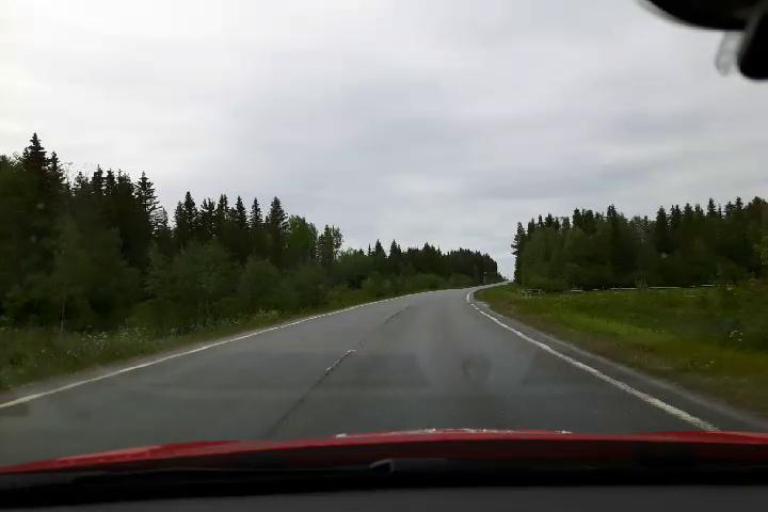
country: SE
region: Jaemtland
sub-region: Bergs Kommun
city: Hoverberg
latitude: 62.9083
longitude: 14.3312
